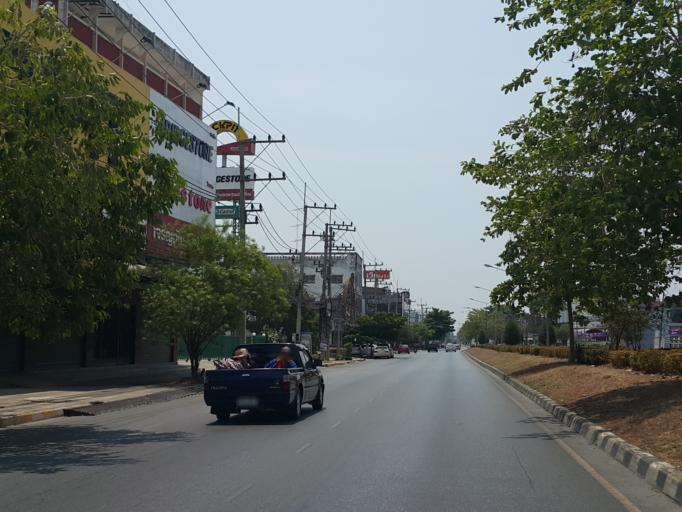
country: TH
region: Kanchanaburi
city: Kanchanaburi
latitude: 14.0379
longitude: 99.5192
